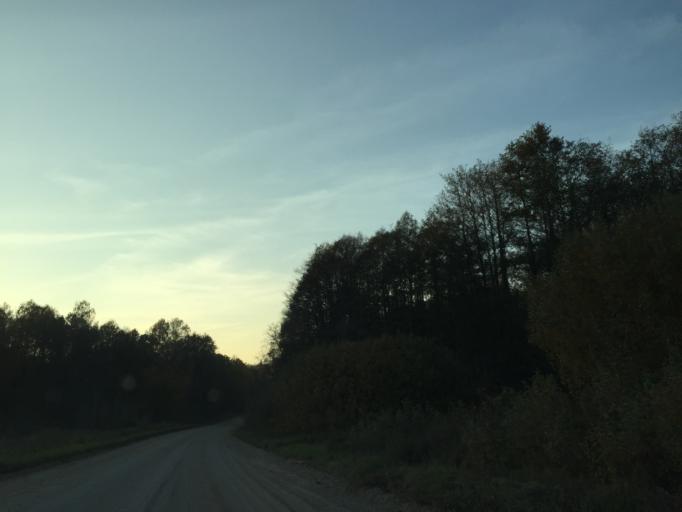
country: LV
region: Priekule
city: Priekule
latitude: 56.4798
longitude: 21.7224
